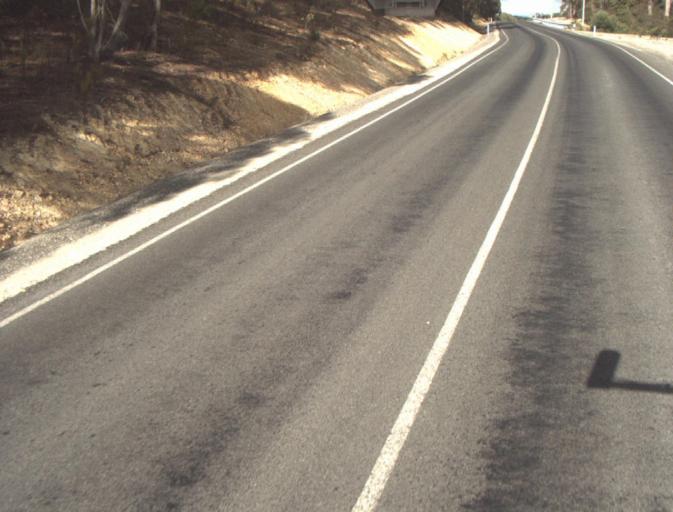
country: AU
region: Tasmania
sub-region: Dorset
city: Bridport
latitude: -41.1659
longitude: 147.2581
